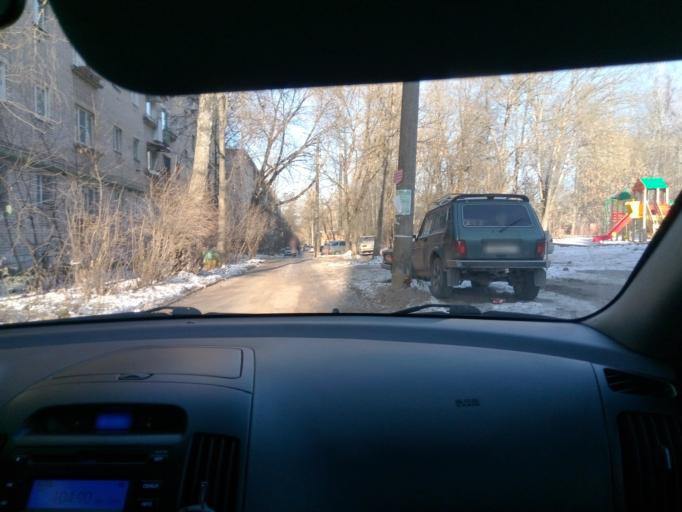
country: RU
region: Tula
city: Mendeleyevskiy
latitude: 54.1651
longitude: 37.5646
